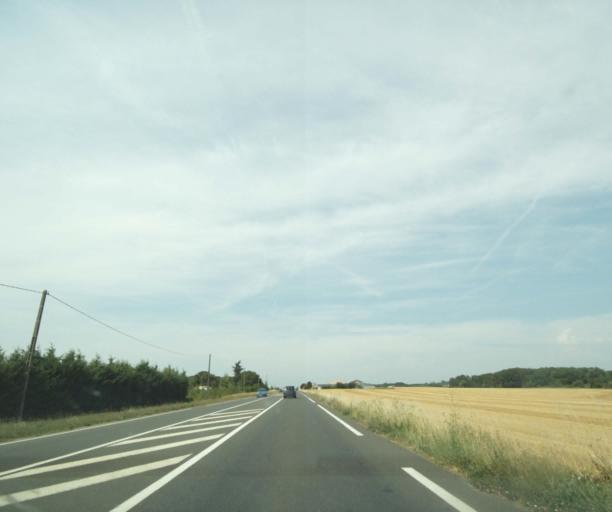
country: FR
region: Centre
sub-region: Departement d'Indre-et-Loire
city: Sorigny
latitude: 47.2512
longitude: 0.6983
